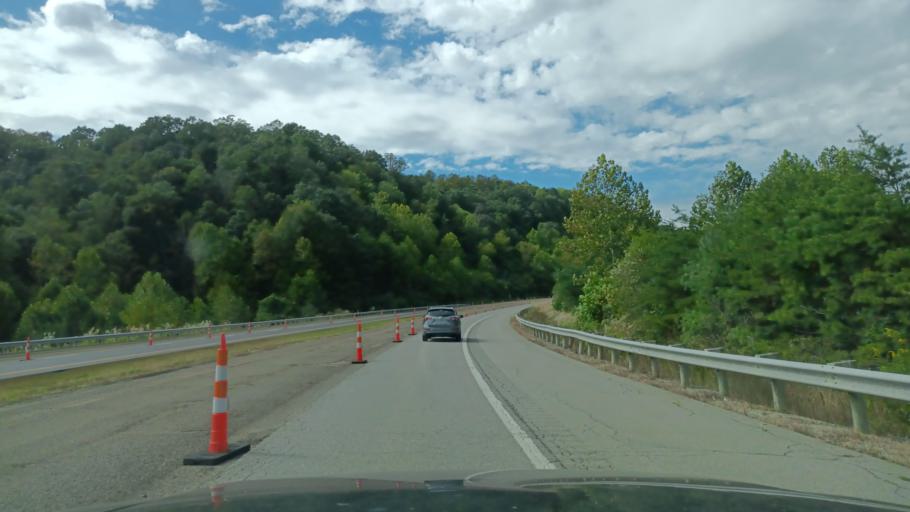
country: US
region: West Virginia
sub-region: Ritchie County
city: Harrisville
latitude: 39.2570
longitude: -81.1112
